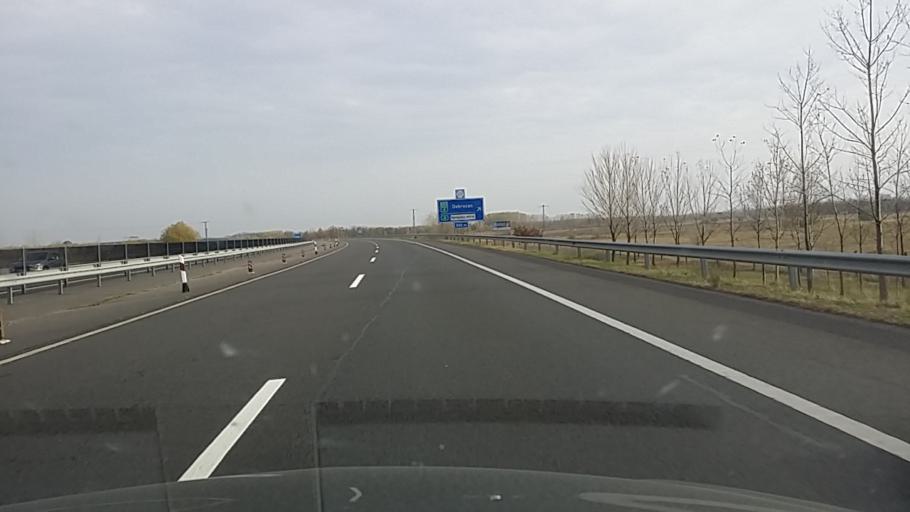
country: HU
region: Szabolcs-Szatmar-Bereg
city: Nyiregyhaza
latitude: 47.8867
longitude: 21.6980
